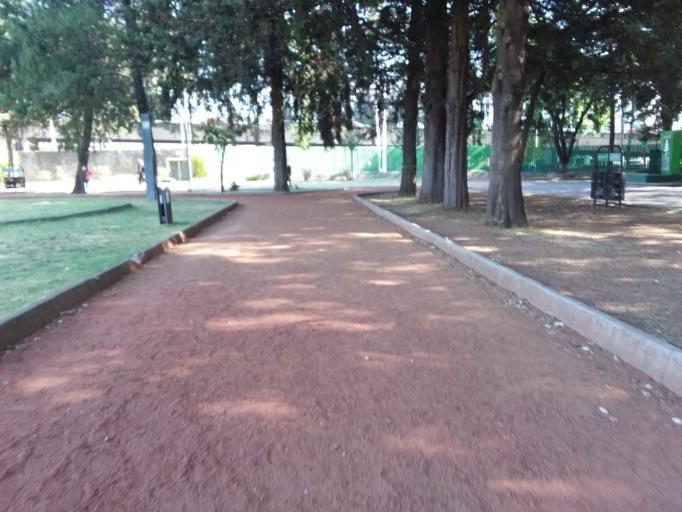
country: MX
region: Mexico
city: Toluca
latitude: 19.2716
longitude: -99.6530
